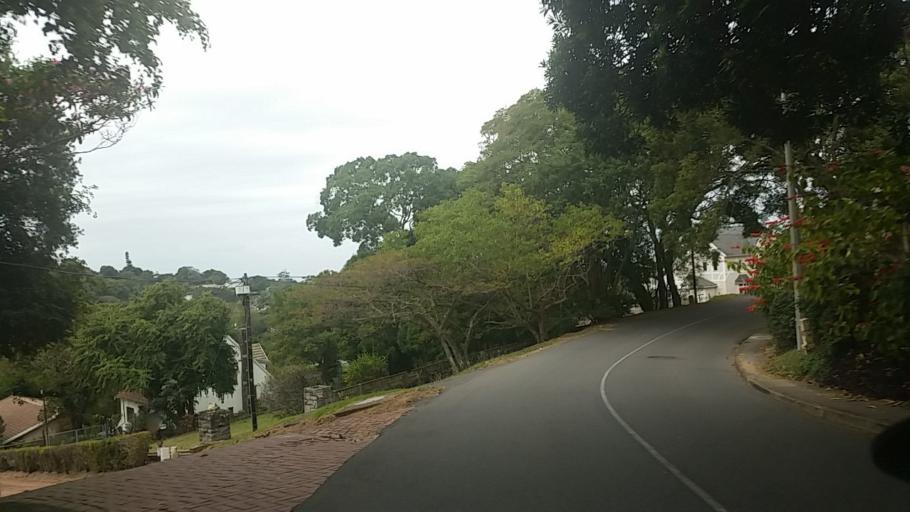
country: ZA
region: KwaZulu-Natal
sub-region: eThekwini Metropolitan Municipality
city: Berea
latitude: -29.8396
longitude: 30.9272
